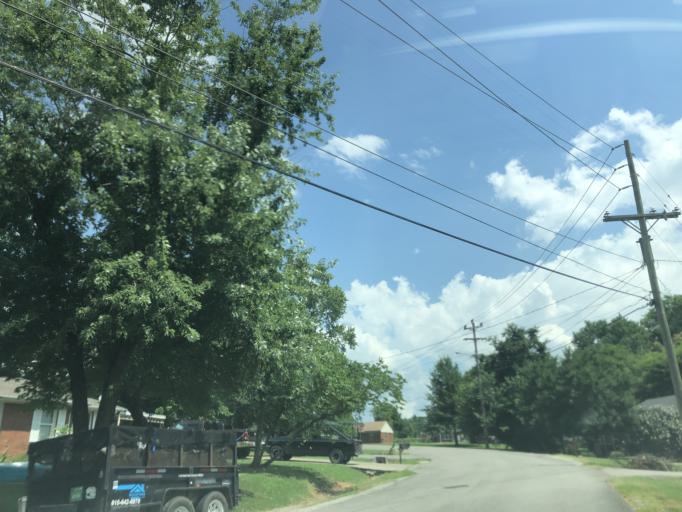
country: US
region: Tennessee
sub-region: Davidson County
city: Lakewood
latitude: 36.1561
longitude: -86.6501
